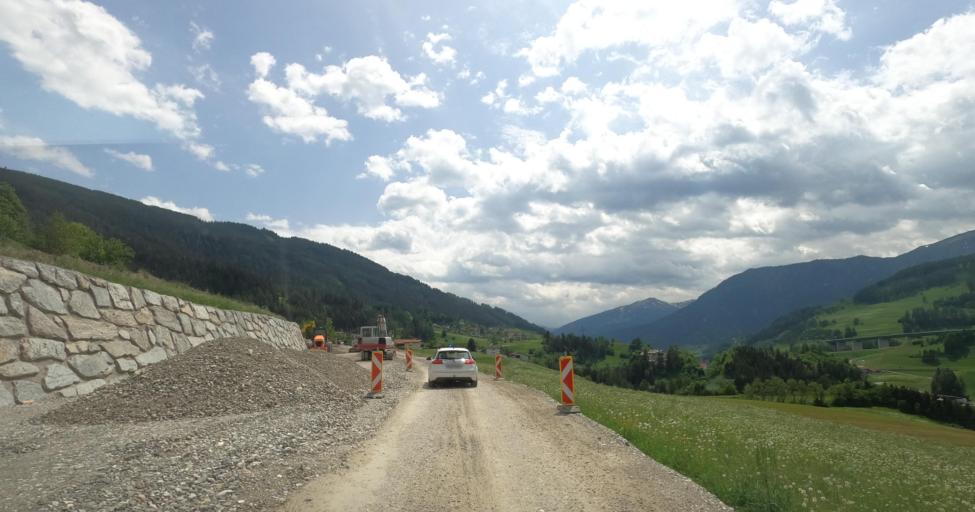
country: AT
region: Tyrol
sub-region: Politischer Bezirk Innsbruck Land
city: Pfons
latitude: 47.1455
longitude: 11.4570
